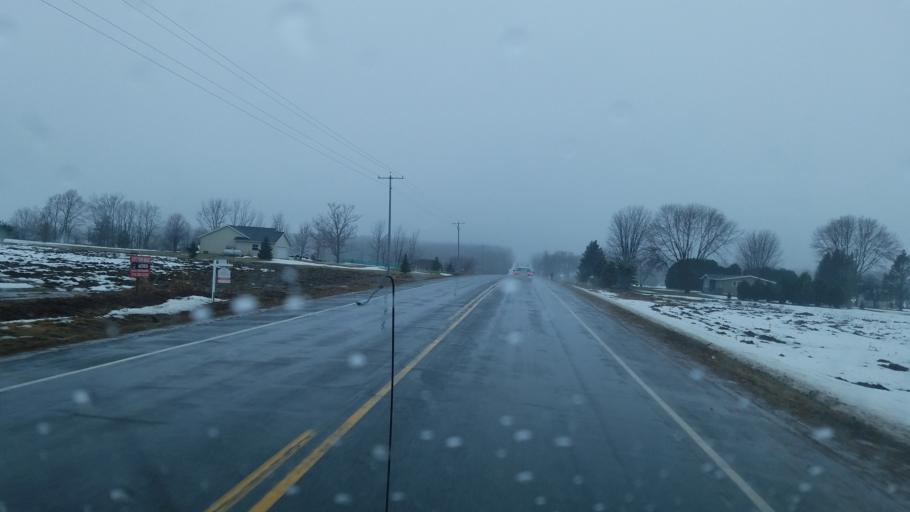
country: US
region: Wisconsin
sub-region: Wood County
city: Marshfield
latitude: 44.6777
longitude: -90.2412
